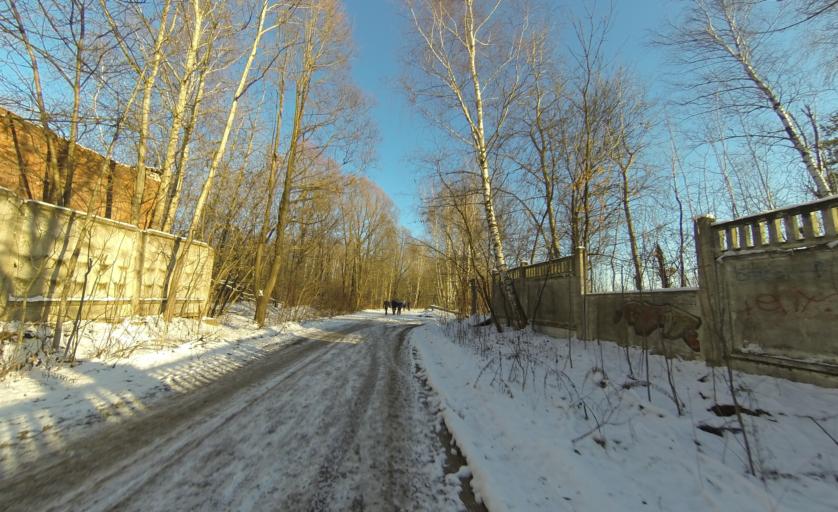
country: RU
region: Moskovskaya
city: Bogorodskoye
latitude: 55.8326
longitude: 37.6953
